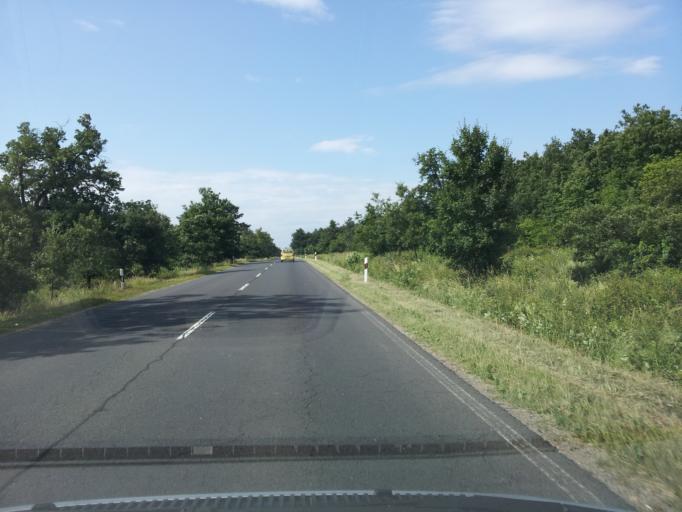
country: HU
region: Veszprem
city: Nemesvamos
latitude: 47.0308
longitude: 17.9118
